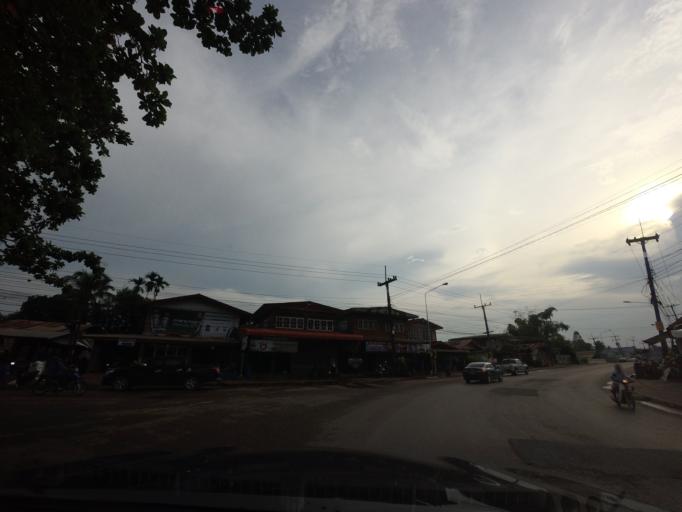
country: TH
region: Changwat Udon Thani
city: Nam Som
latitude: 17.8021
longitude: 102.2832
